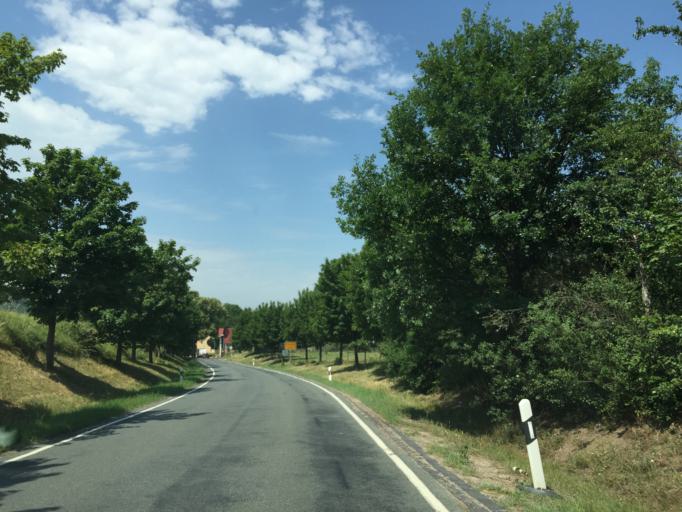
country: DE
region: Thuringia
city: Barchfeld
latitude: 50.8000
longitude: 11.1737
